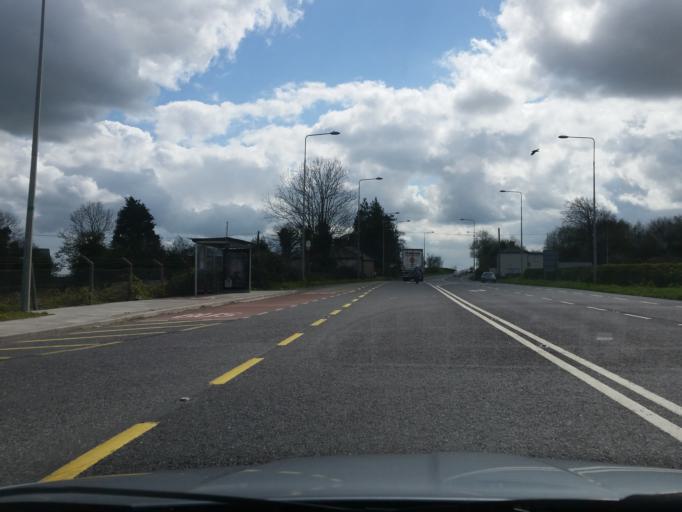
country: IE
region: Leinster
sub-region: An Mhi
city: Ratoath
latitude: 53.5723
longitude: -6.4493
